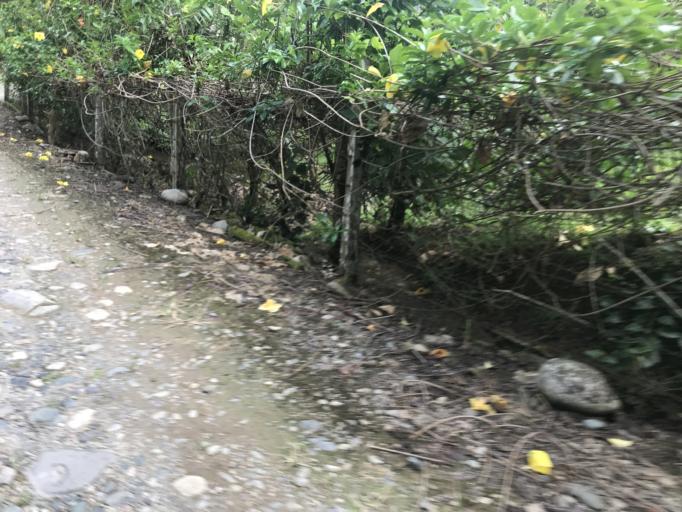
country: EC
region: Napo
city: Tena
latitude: -1.0522
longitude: -77.7728
